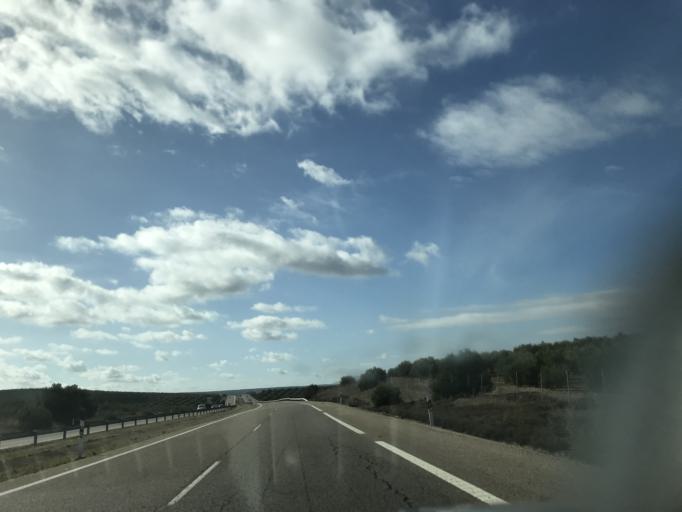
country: ES
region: Andalusia
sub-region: Province of Cordoba
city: Villa del Rio
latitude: 38.0037
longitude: -4.2367
